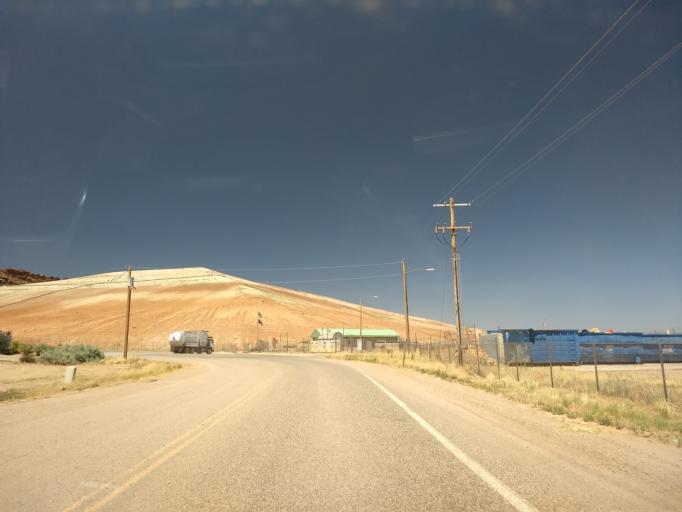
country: US
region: Utah
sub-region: Washington County
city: Washington
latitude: 37.1364
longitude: -113.4506
